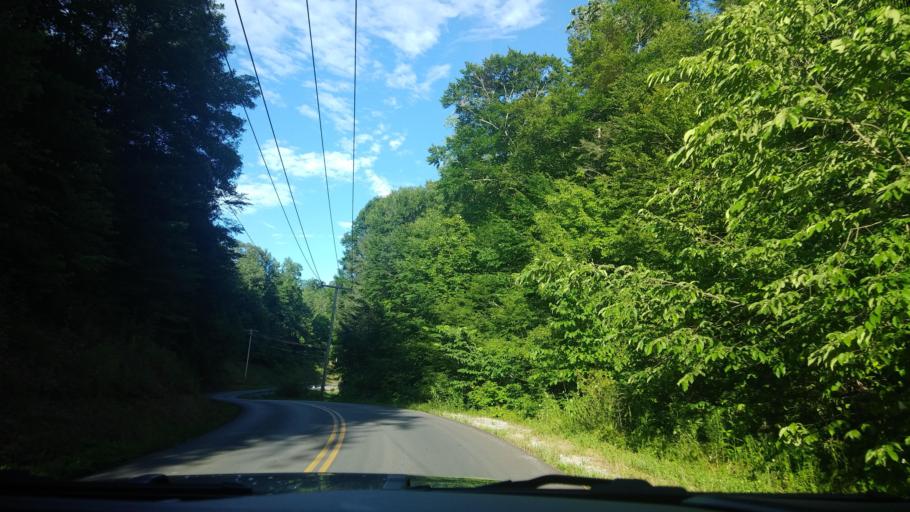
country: US
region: Tennessee
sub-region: Sevier County
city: Pigeon Forge
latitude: 35.7668
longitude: -83.5997
